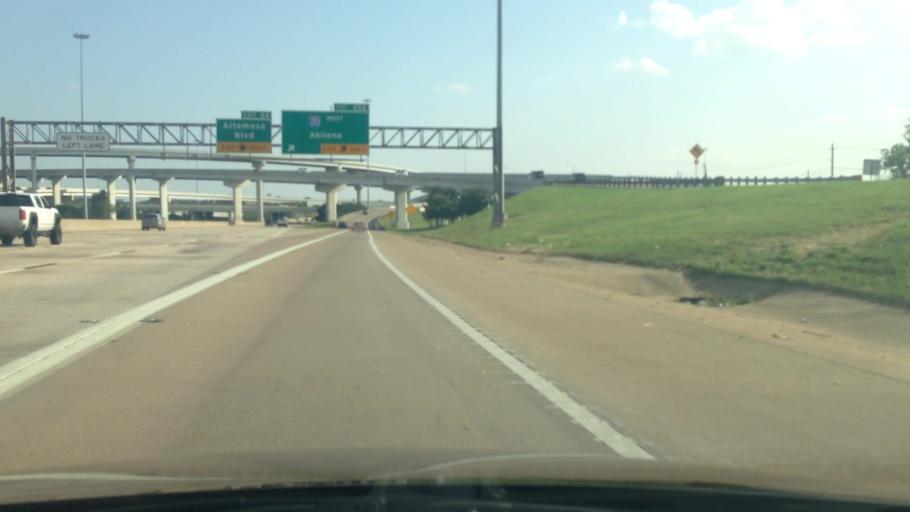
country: US
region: Texas
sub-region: Tarrant County
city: Edgecliff Village
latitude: 32.6716
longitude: -97.3207
